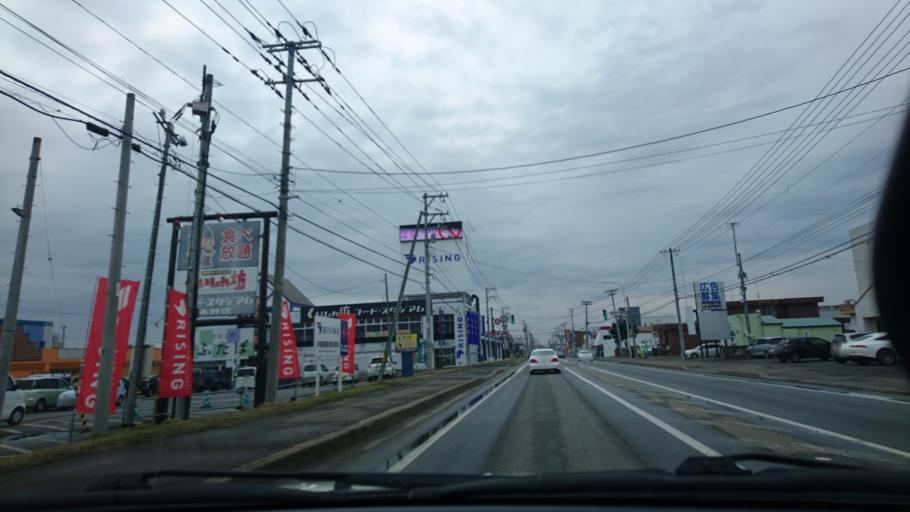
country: JP
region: Hokkaido
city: Otofuke
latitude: 42.9552
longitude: 143.2058
